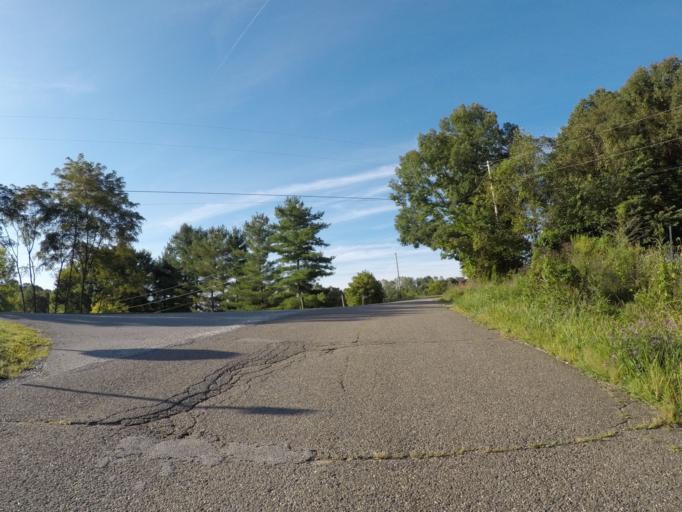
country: US
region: Ohio
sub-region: Lawrence County
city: Coal Grove
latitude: 38.5856
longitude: -82.5515
